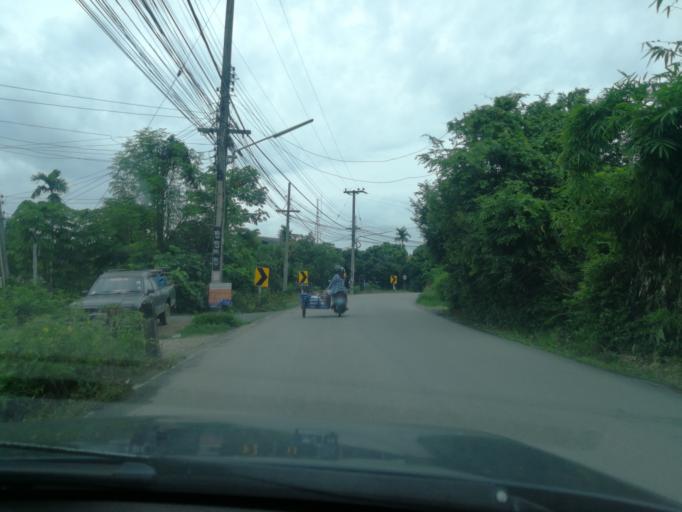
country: TH
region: Chiang Mai
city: San Pa Tong
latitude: 18.6023
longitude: 98.9074
